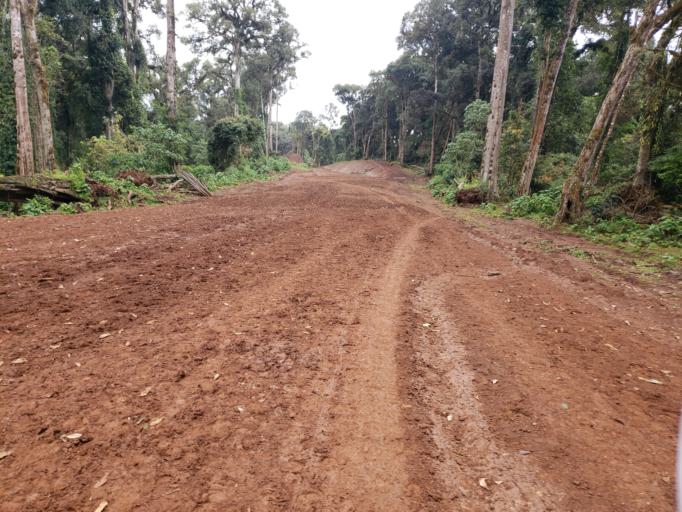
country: ET
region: Oromiya
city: Dodola
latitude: 6.5874
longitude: 39.4125
